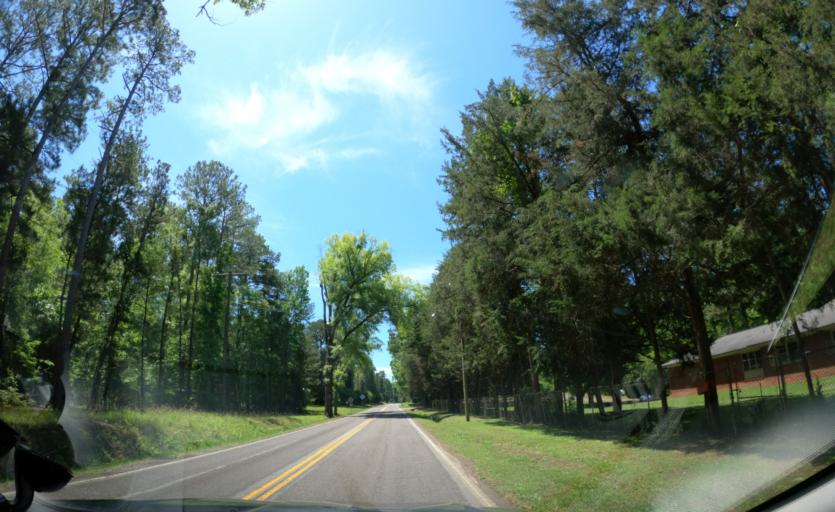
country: US
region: South Carolina
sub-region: Abbeville County
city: Calhoun Falls
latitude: 34.0102
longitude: -82.5072
